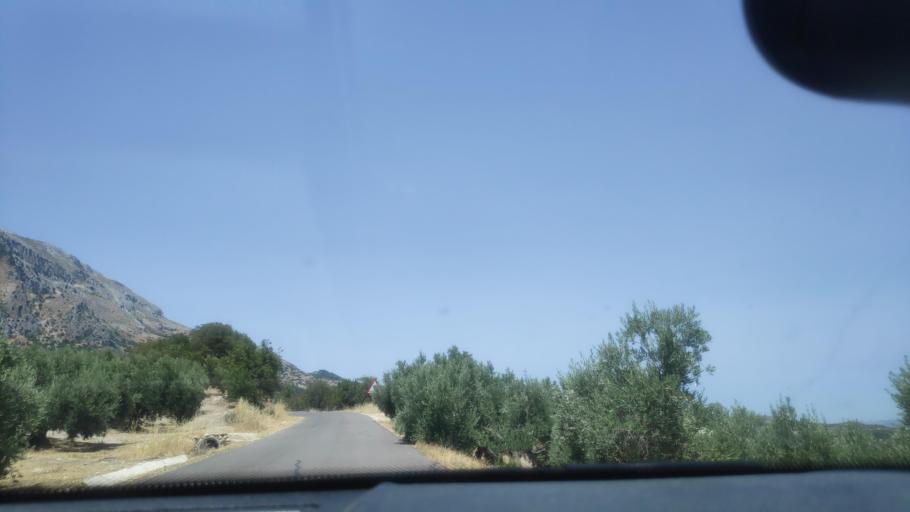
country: ES
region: Andalusia
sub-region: Provincia de Jaen
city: Jimena
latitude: 37.7997
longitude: -3.4484
